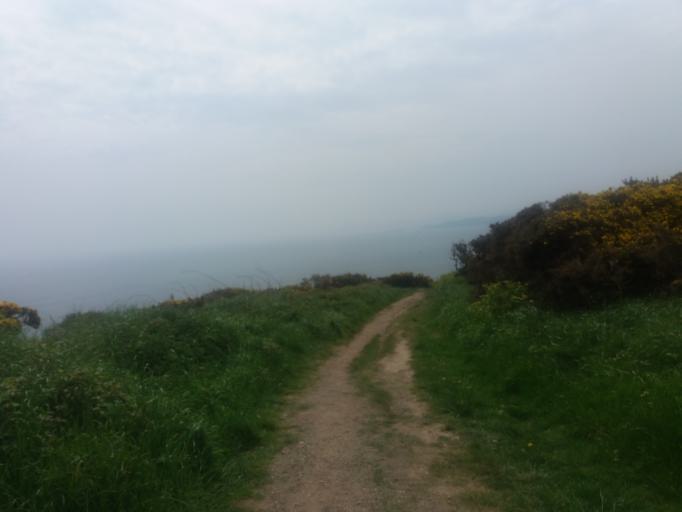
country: IE
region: Leinster
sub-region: Fingal County
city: Howth
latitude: 53.3699
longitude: -6.0556
